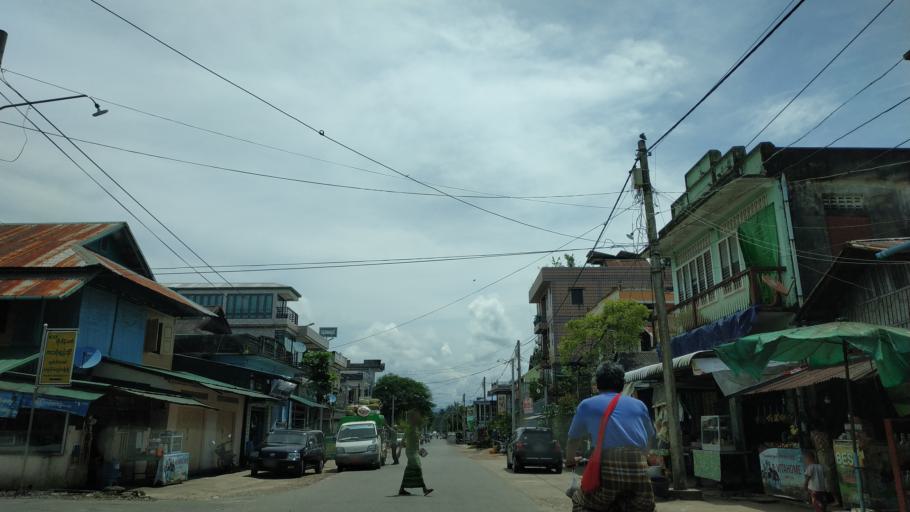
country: MM
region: Tanintharyi
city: Dawei
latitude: 14.0694
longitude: 98.1919
